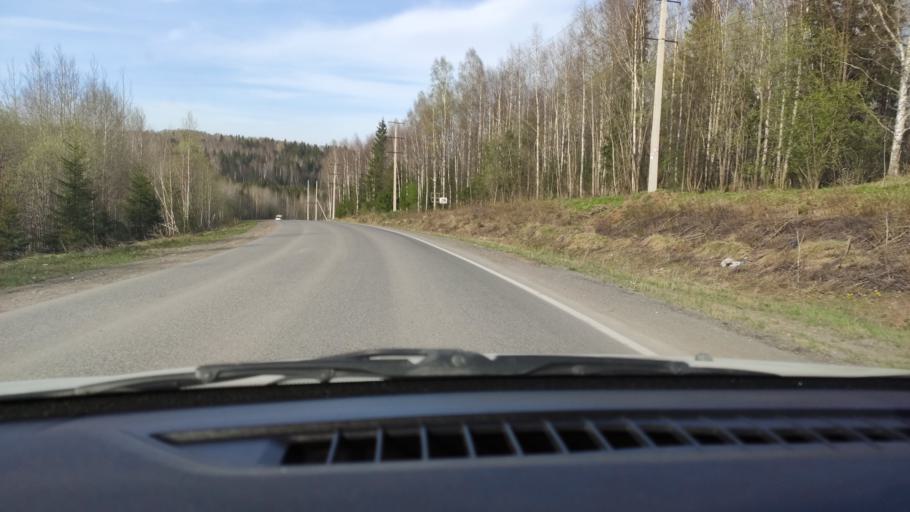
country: RU
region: Perm
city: Novyye Lyady
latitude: 57.9566
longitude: 56.5343
